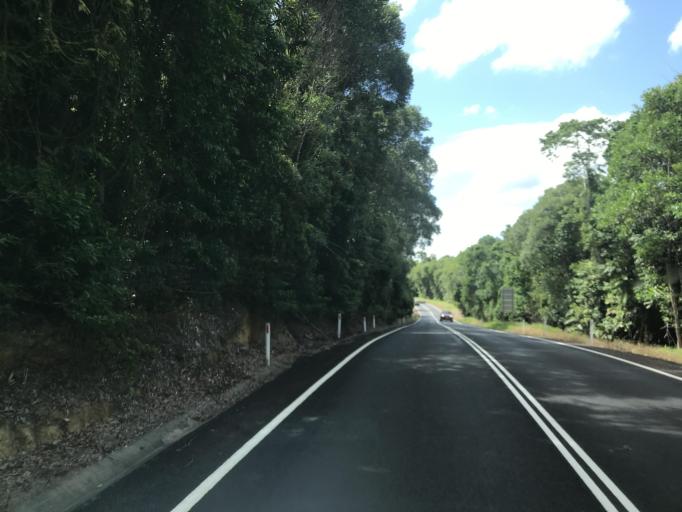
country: AU
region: Queensland
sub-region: Cassowary Coast
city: Innisfail
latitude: -17.8638
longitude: 146.0659
